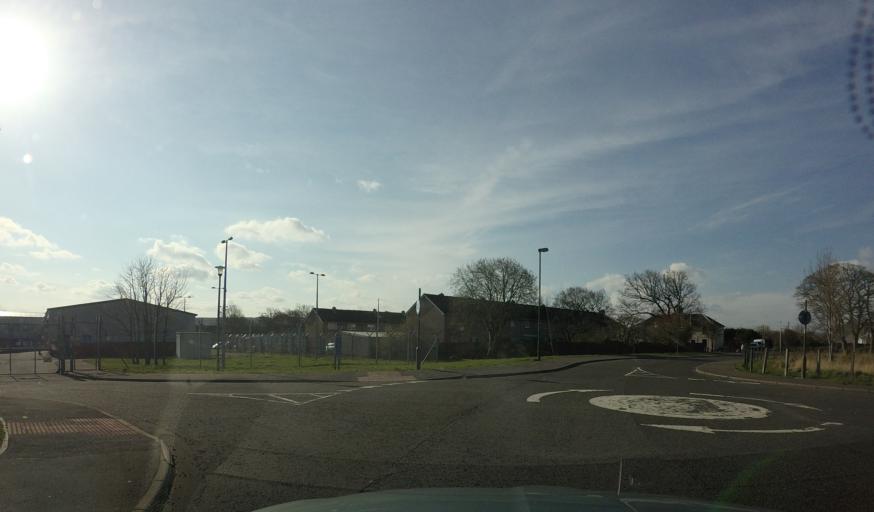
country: GB
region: Scotland
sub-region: Midlothian
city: Penicuik
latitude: 55.8484
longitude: -3.2063
